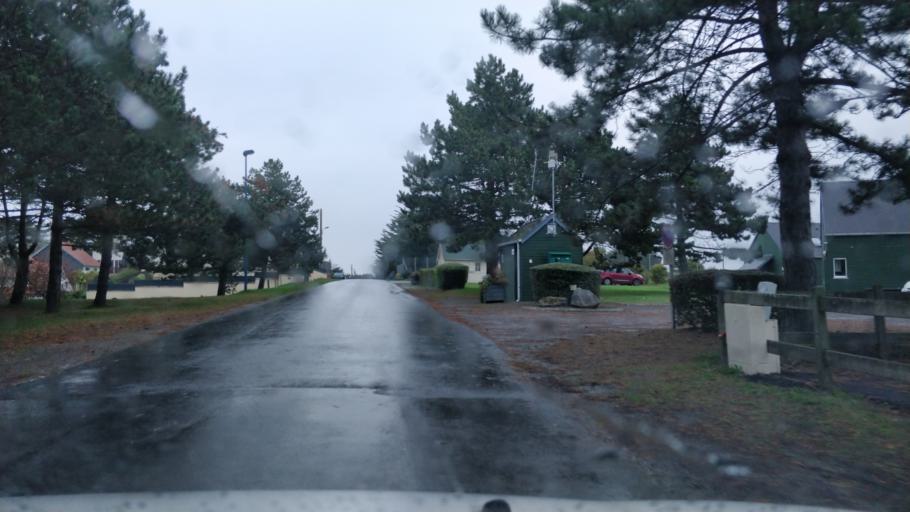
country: FR
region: Lower Normandy
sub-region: Departement de la Manche
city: Brehal
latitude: 48.8984
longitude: -1.5655
